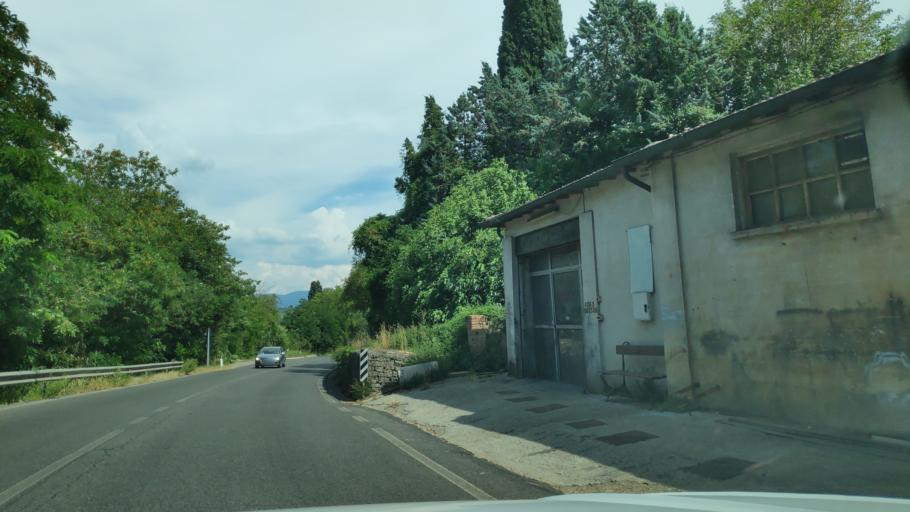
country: IT
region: Umbria
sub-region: Provincia di Terni
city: Orvieto
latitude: 42.7264
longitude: 12.1192
